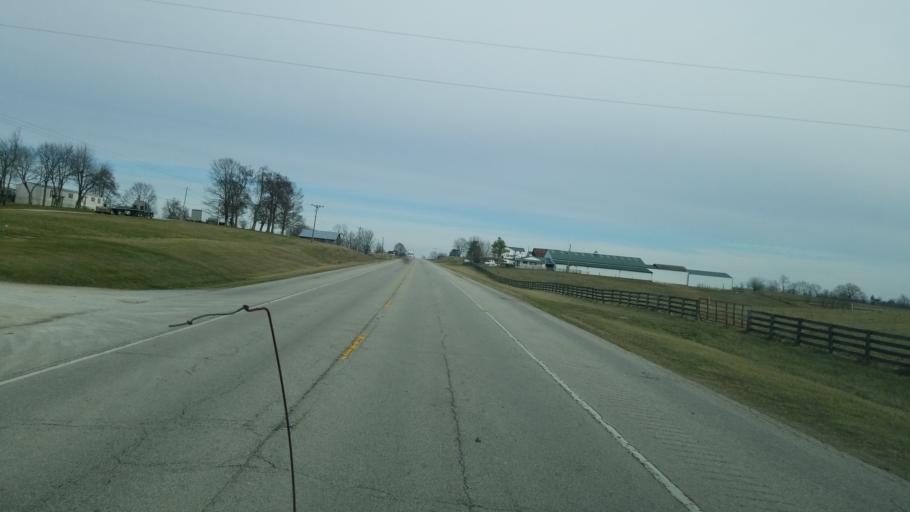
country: US
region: Kentucky
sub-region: Fleming County
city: Flemingsburg
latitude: 38.4801
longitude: -83.8752
